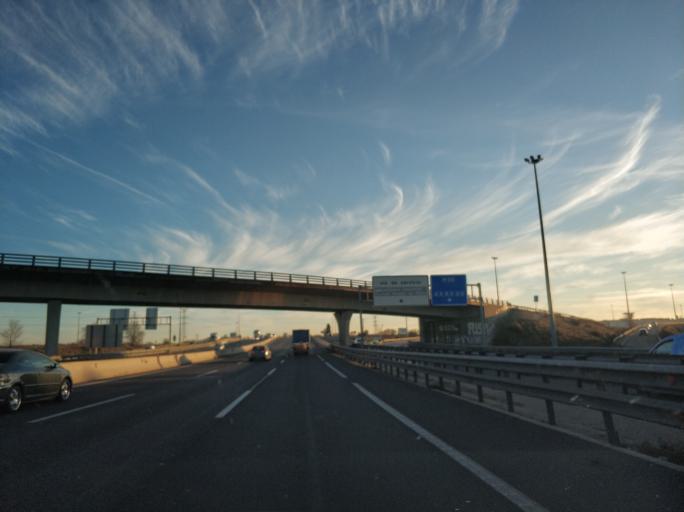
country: ES
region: Madrid
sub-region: Provincia de Madrid
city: Pinto
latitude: 40.2792
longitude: -3.6911
